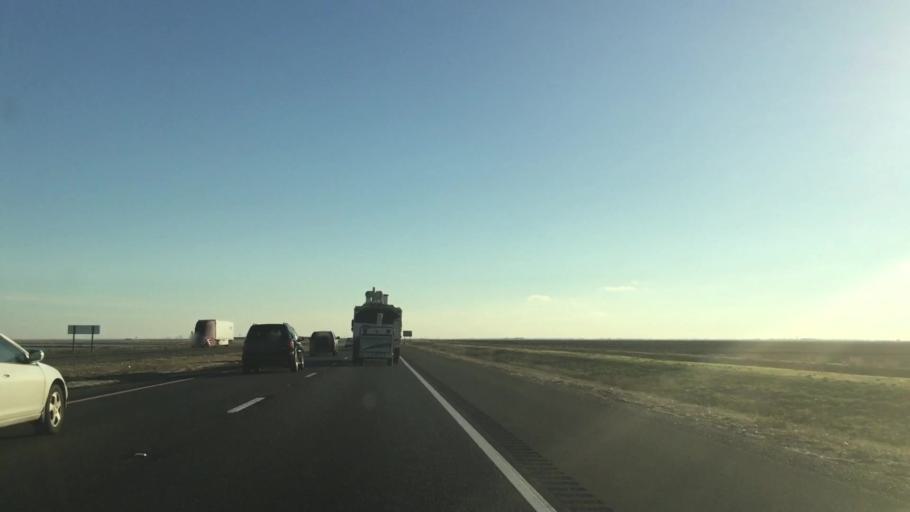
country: US
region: California
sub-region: Sacramento County
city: Elverta
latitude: 38.7733
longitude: -121.5438
